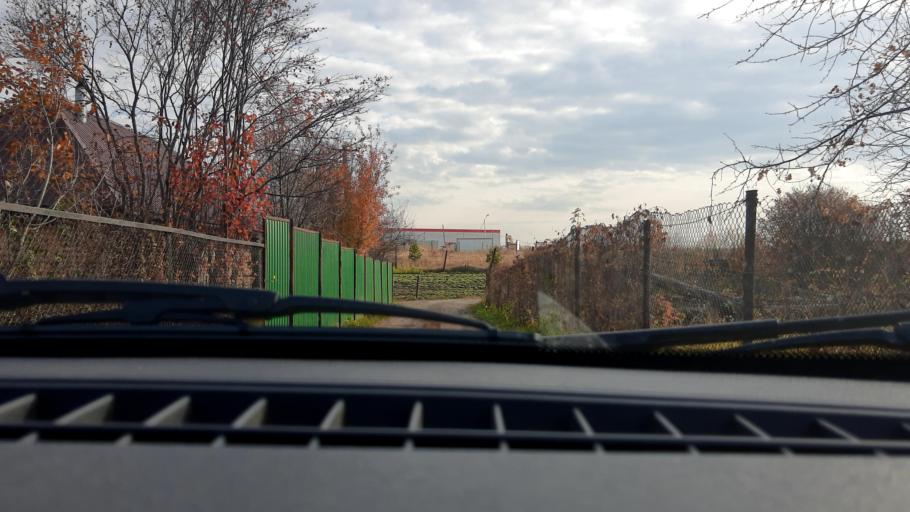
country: RU
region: Bashkortostan
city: Ufa
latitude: 54.6002
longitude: 55.8964
